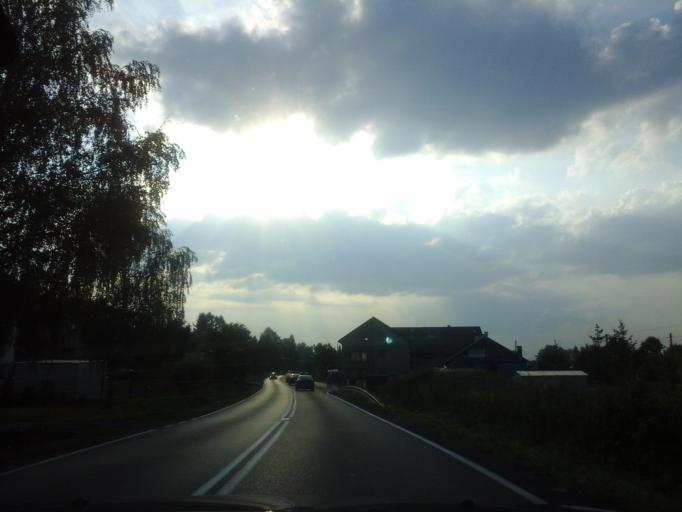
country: PL
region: Lesser Poland Voivodeship
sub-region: Powiat wadowicki
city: Brzeznica
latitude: 49.9644
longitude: 19.6430
